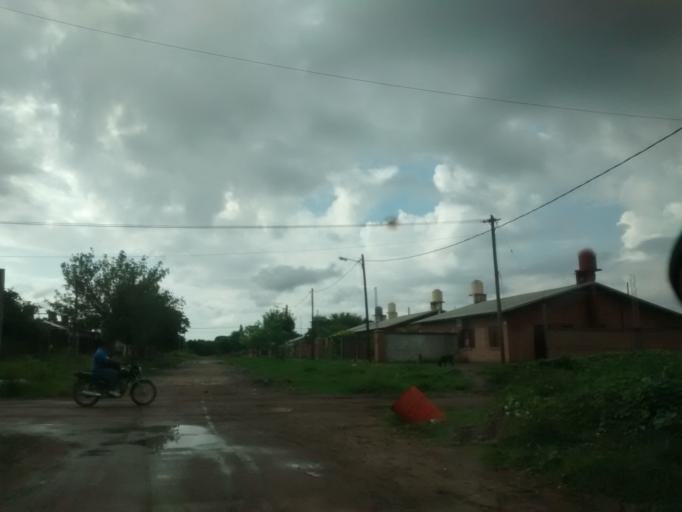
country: AR
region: Chaco
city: Puerto Tirol
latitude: -27.3801
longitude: -59.0917
